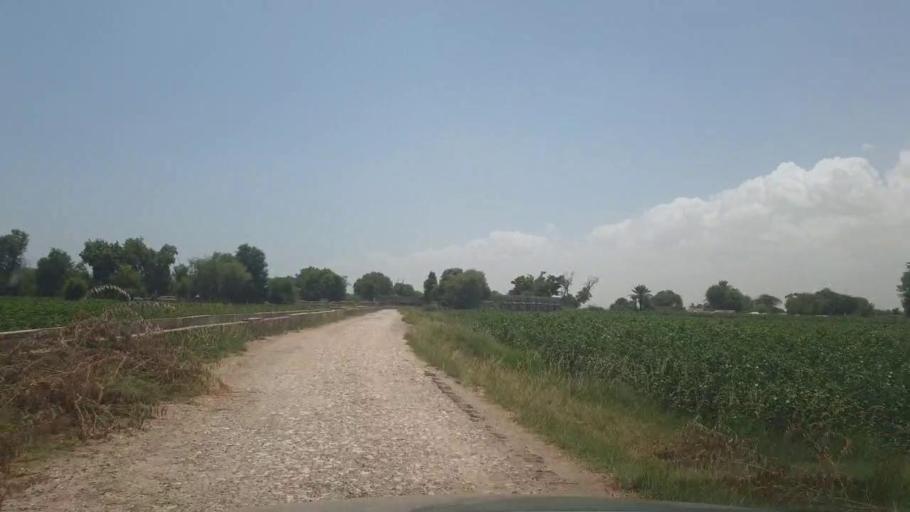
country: PK
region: Sindh
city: Kot Diji
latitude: 27.2665
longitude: 69.0186
